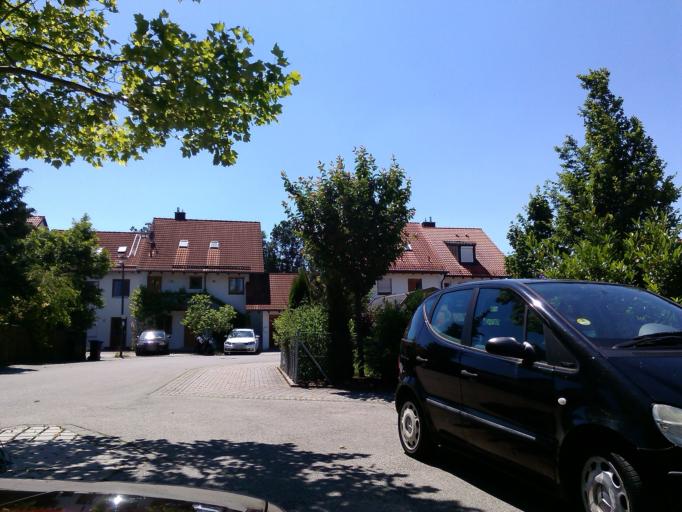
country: DE
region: Bavaria
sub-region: Upper Bavaria
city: Gilching
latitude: 48.1063
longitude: 11.2875
